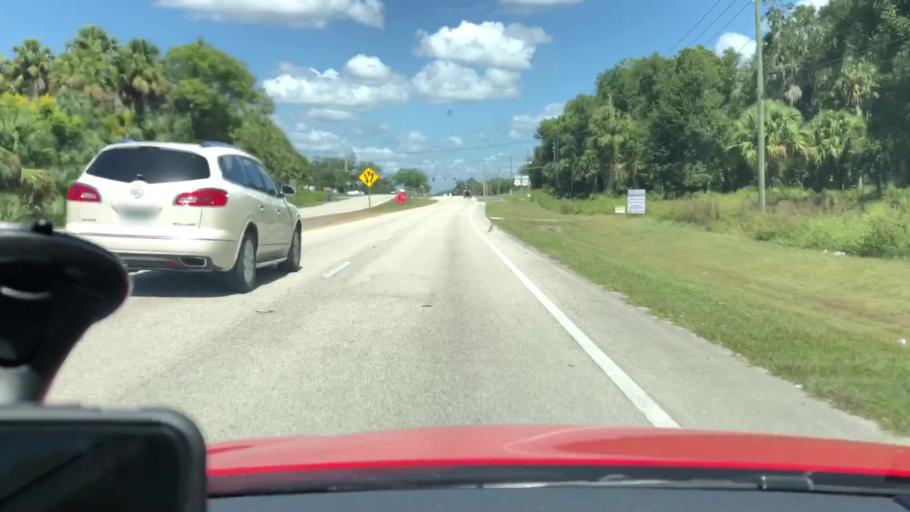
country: US
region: Florida
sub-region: Volusia County
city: Orange City
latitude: 28.9607
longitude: -81.2987
